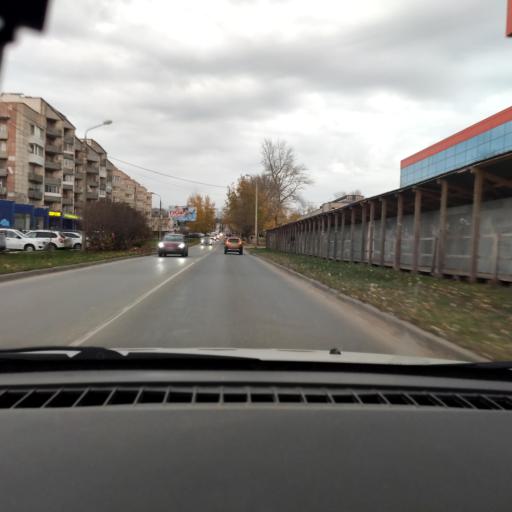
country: RU
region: Perm
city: Perm
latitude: 58.1102
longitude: 56.3718
